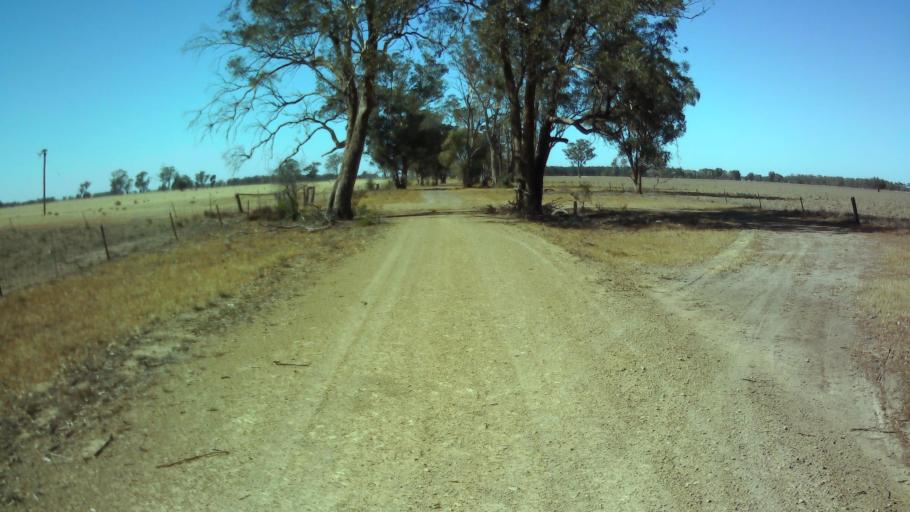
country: AU
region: New South Wales
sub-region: Weddin
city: Grenfell
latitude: -33.9462
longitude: 147.8700
